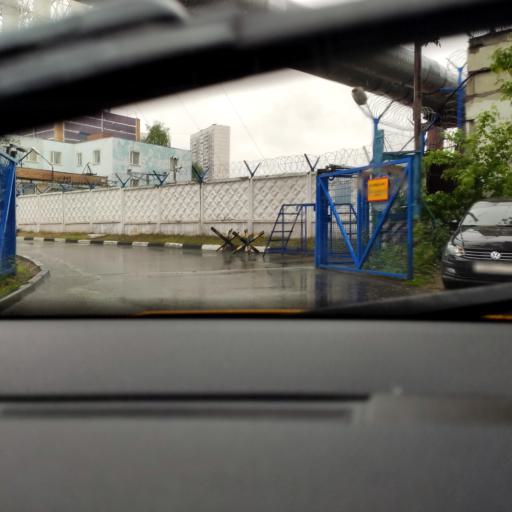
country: RU
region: Moscow
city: Strogino
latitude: 55.8409
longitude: 37.4268
